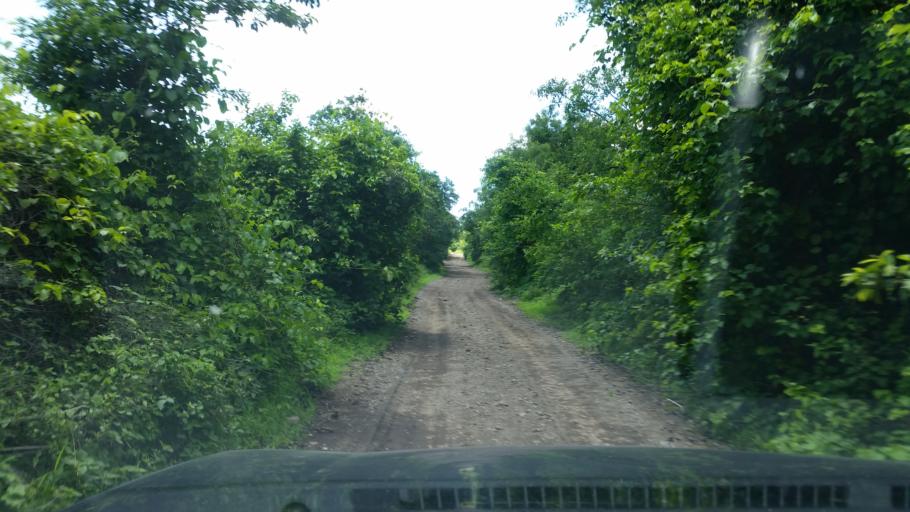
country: NI
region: Chinandega
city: Puerto Morazan
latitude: 12.7608
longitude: -87.1273
